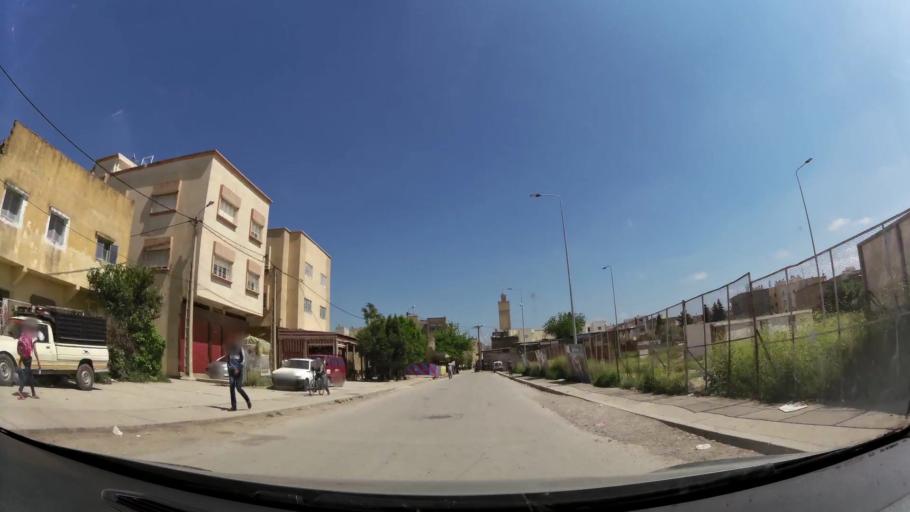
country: MA
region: Fes-Boulemane
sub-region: Fes
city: Fes
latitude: 34.0144
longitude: -5.0309
